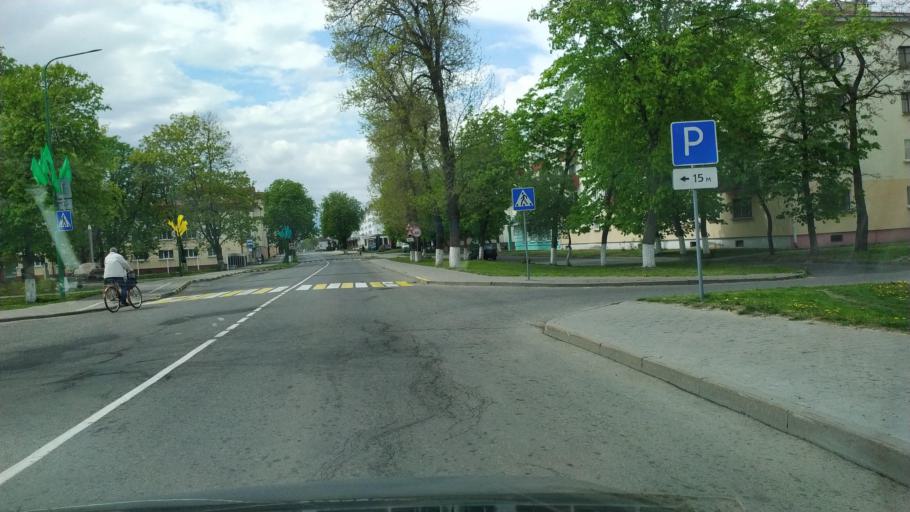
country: BY
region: Brest
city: Pruzhany
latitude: 52.5543
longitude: 24.4657
